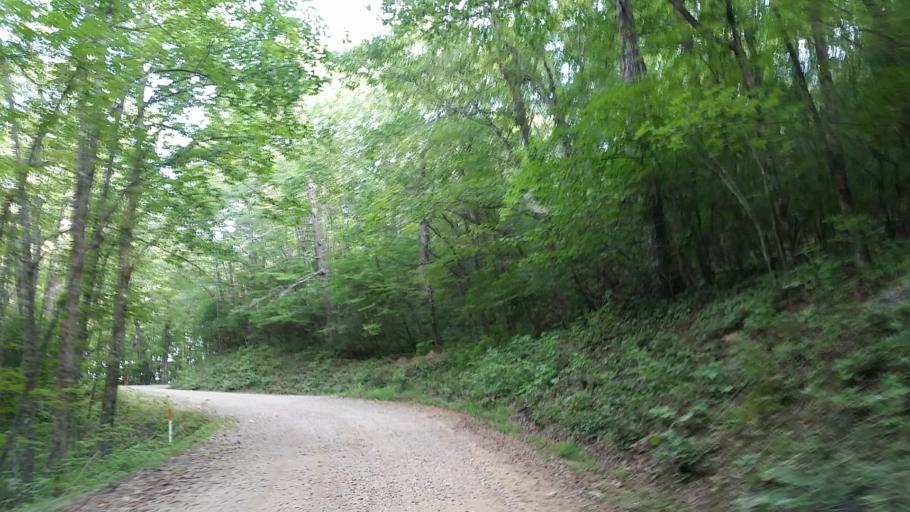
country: US
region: Georgia
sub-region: Lumpkin County
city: Dahlonega
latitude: 34.6505
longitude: -84.0342
